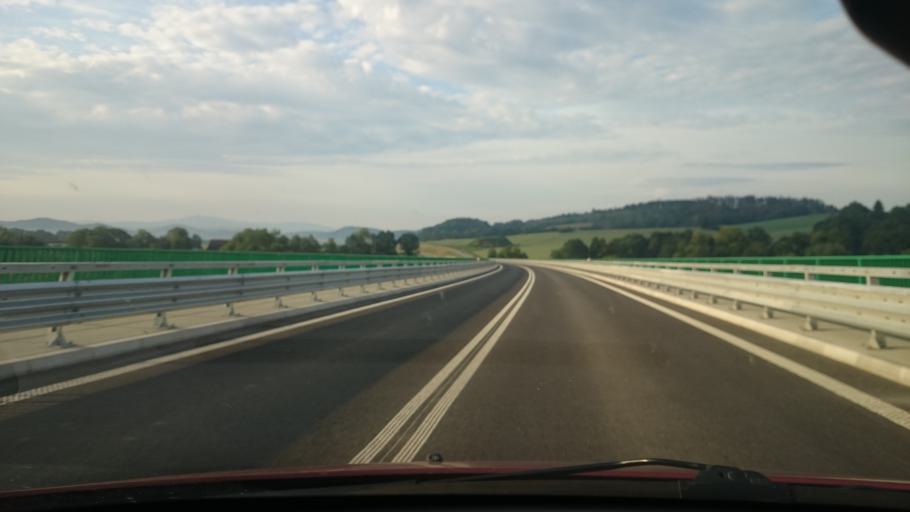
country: PL
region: Lower Silesian Voivodeship
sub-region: Powiat klodzki
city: Klodzko
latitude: 50.4161
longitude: 16.6253
